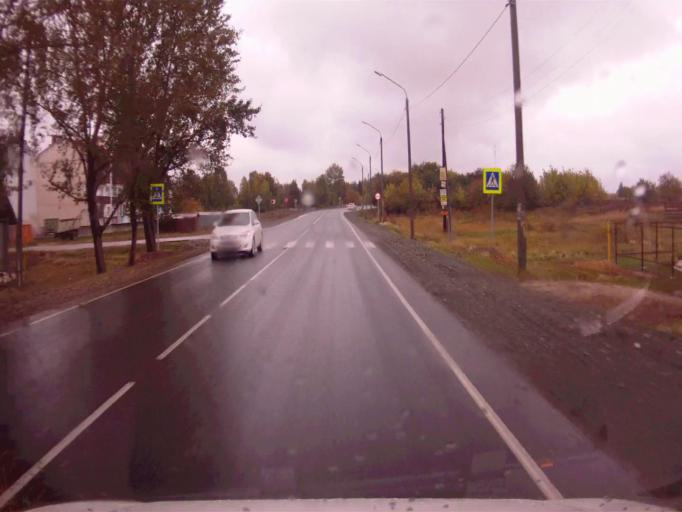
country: RU
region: Chelyabinsk
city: Tayginka
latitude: 55.4970
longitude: 60.6461
